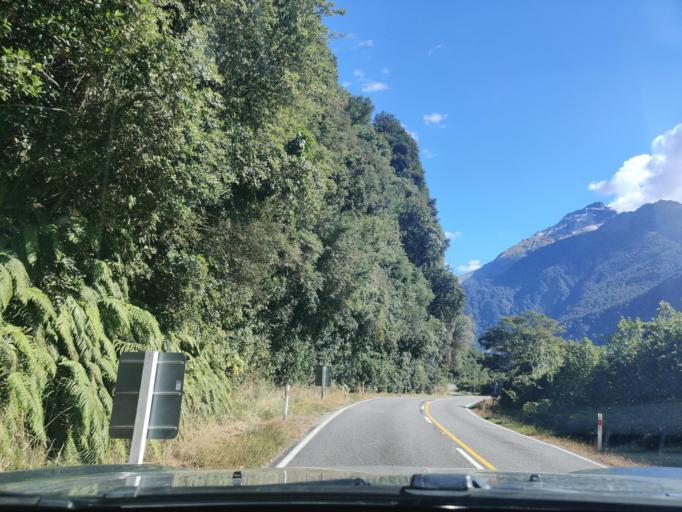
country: NZ
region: Otago
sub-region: Queenstown-Lakes District
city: Wanaka
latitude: -43.9750
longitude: 169.4239
